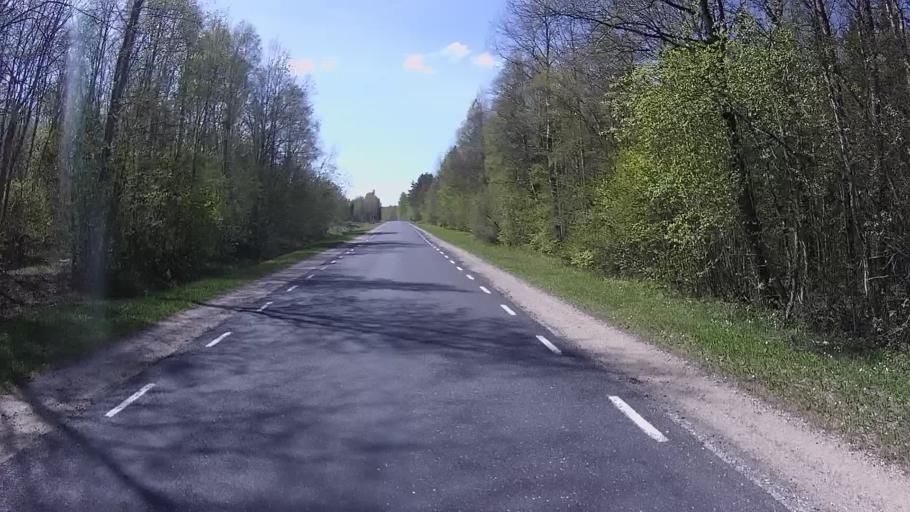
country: EE
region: Laeaene
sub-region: Ridala Parish
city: Uuemoisa
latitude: 59.0272
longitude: 23.8118
